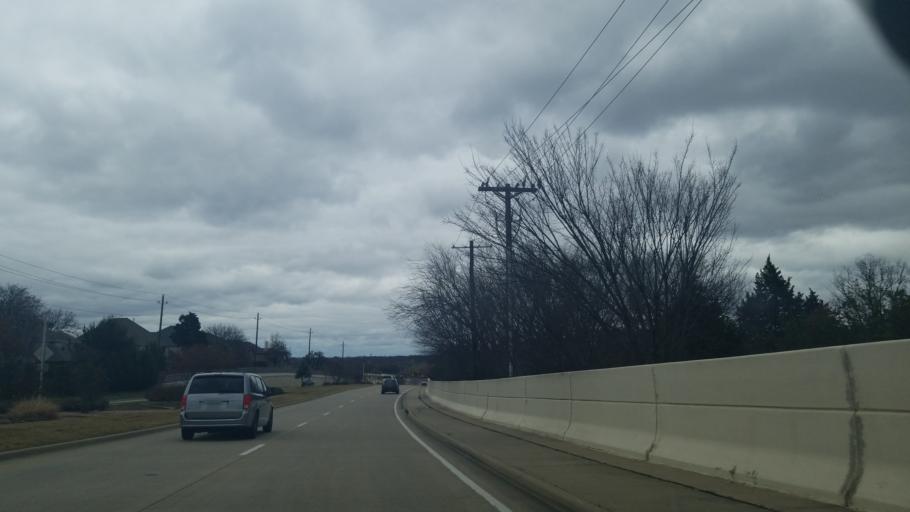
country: US
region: Texas
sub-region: Denton County
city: Copper Canyon
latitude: 33.0979
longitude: -97.0802
